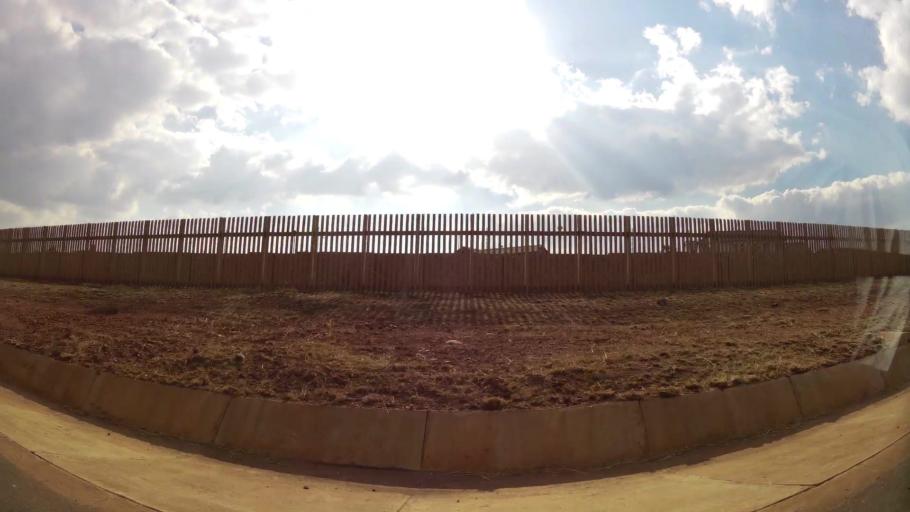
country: ZA
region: Gauteng
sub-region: Ekurhuleni Metropolitan Municipality
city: Tembisa
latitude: -25.9306
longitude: 28.2105
